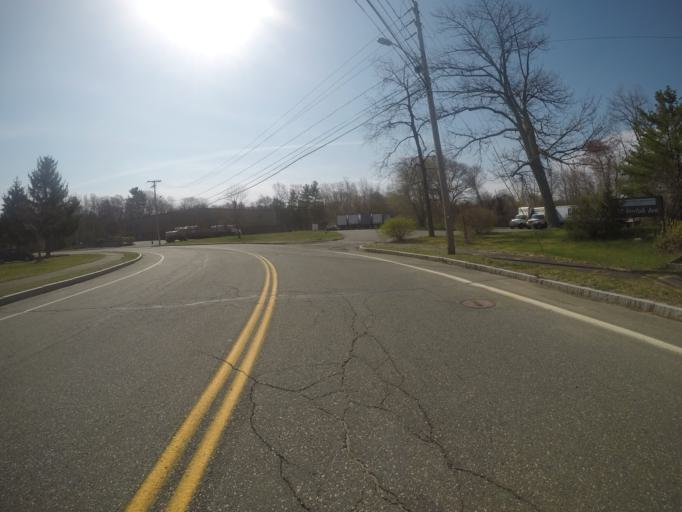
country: US
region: Massachusetts
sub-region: Bristol County
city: Easton
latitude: 42.0441
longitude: -71.0764
